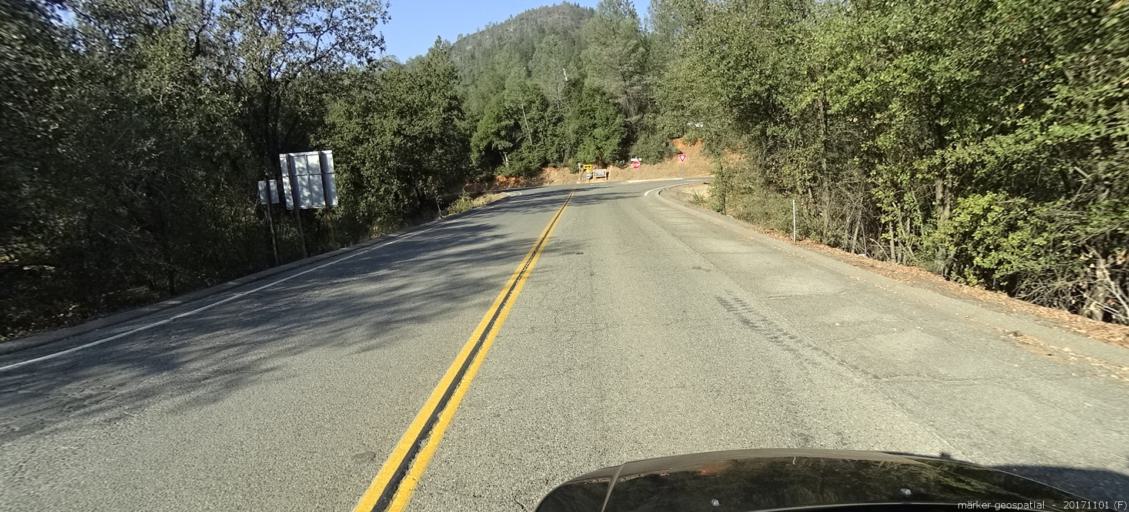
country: US
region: California
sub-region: Shasta County
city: Shasta Lake
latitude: 40.7316
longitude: -122.3223
